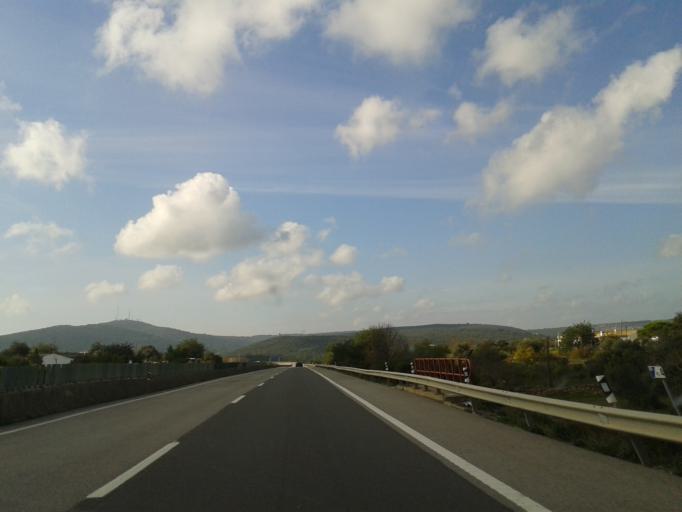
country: PT
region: Faro
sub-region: Olhao
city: Moncarapacho
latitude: 37.1200
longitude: -7.7844
